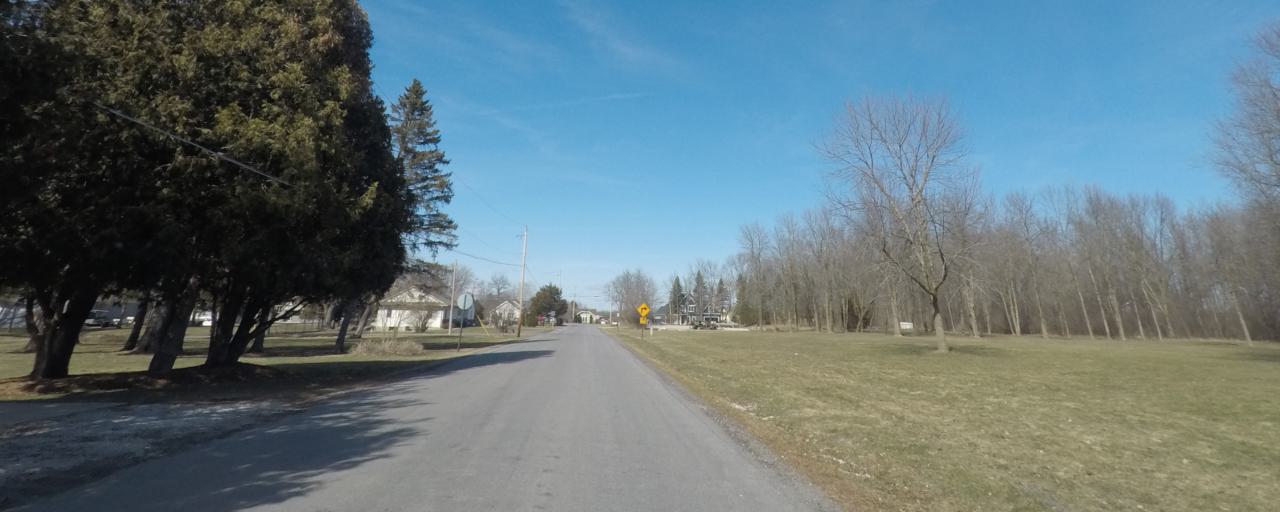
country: US
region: Wisconsin
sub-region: Waukesha County
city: Merton
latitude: 43.1600
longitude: -88.3214
